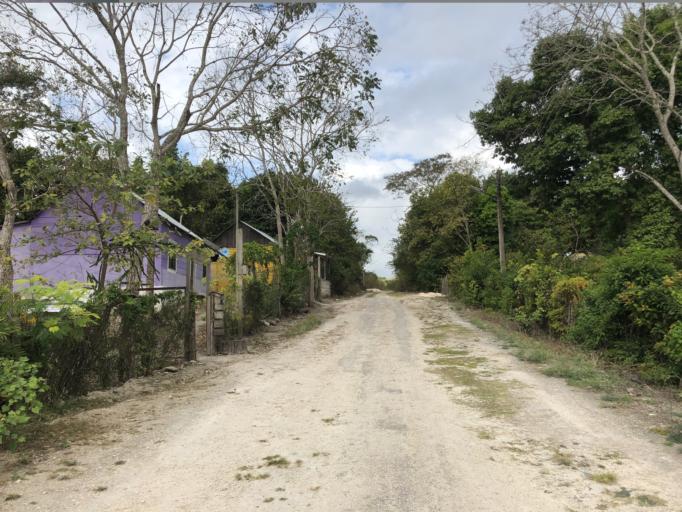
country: MX
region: Quintana Roo
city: Nicolas Bravo
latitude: 18.4502
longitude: -89.3075
